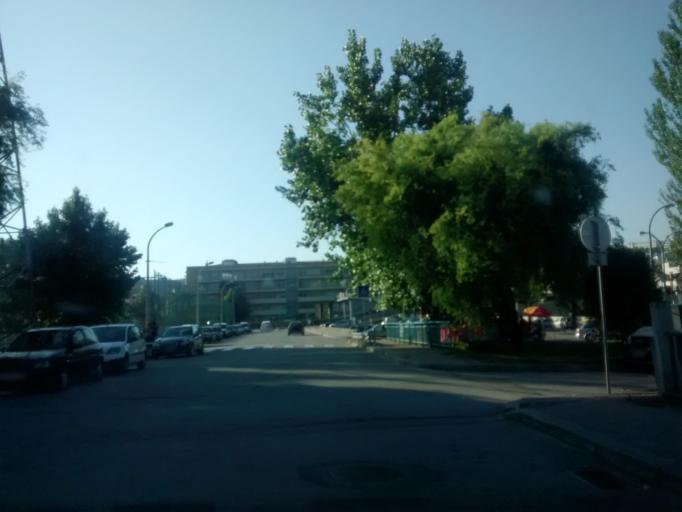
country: PT
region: Braga
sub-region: Braga
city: Braga
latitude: 41.5538
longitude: -8.4002
